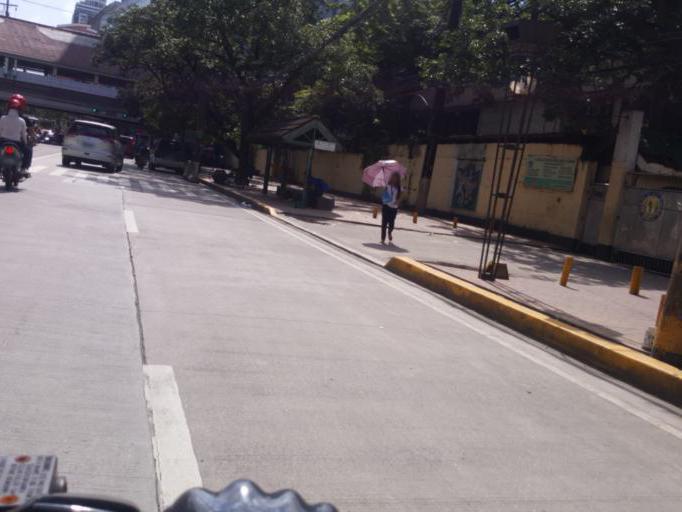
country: PH
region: Metro Manila
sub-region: City of Manila
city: Quiapo
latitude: 14.5828
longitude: 120.9856
